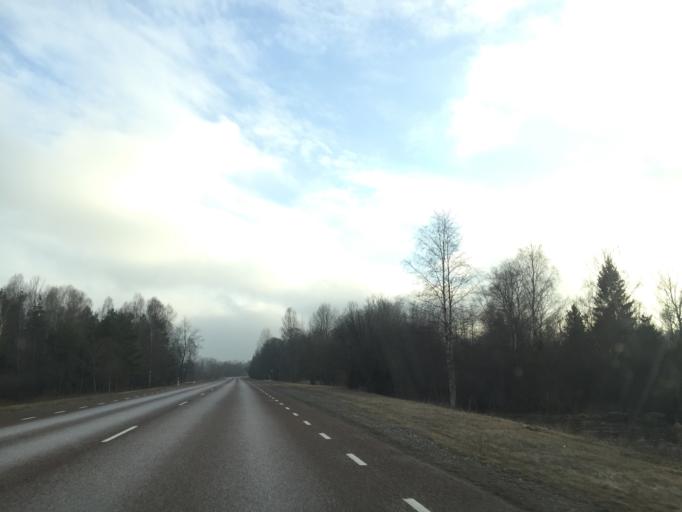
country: EE
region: Saare
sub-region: Kuressaare linn
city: Kuressaare
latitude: 58.3649
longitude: 22.7204
